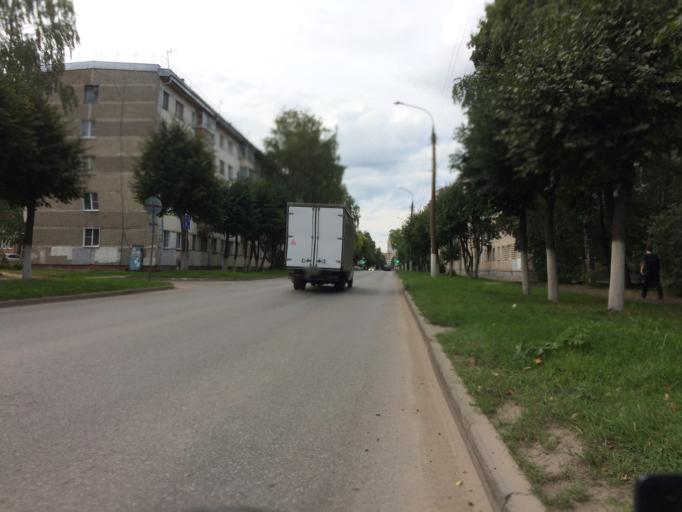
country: RU
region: Mariy-El
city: Yoshkar-Ola
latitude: 56.6343
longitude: 47.8726
